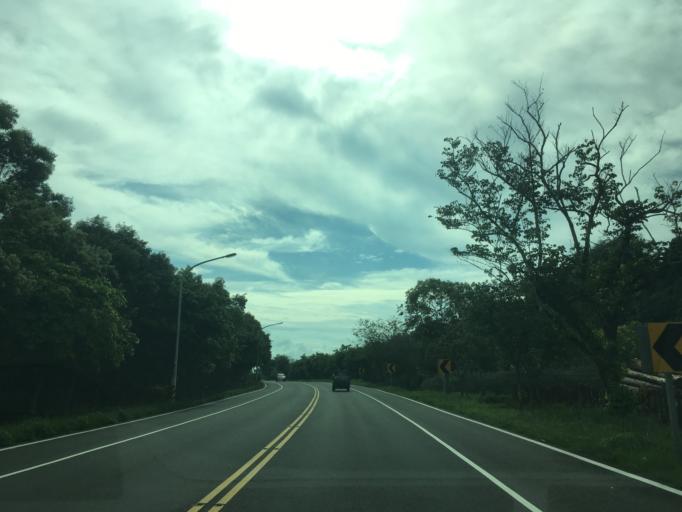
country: TW
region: Taiwan
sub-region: Chiayi
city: Jiayi Shi
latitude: 23.4523
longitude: 120.5647
